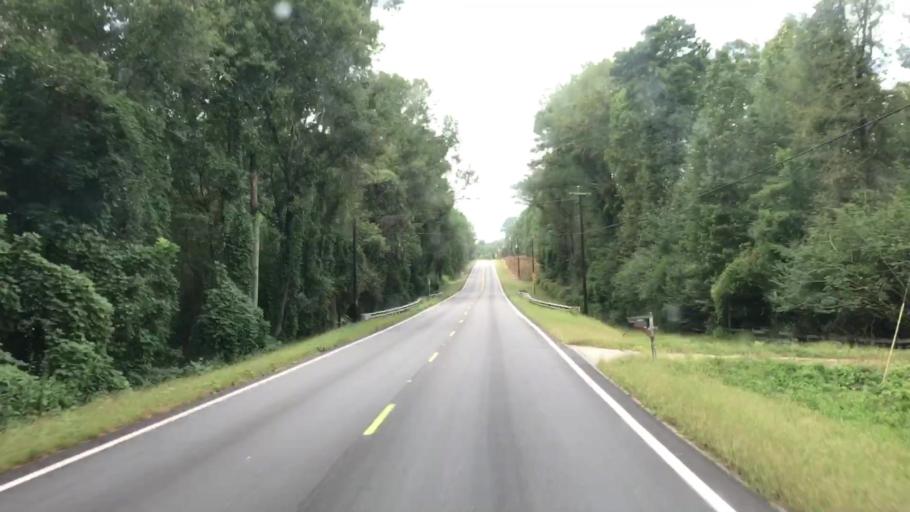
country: US
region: Georgia
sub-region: Greene County
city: Greensboro
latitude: 33.5571
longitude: -83.1150
